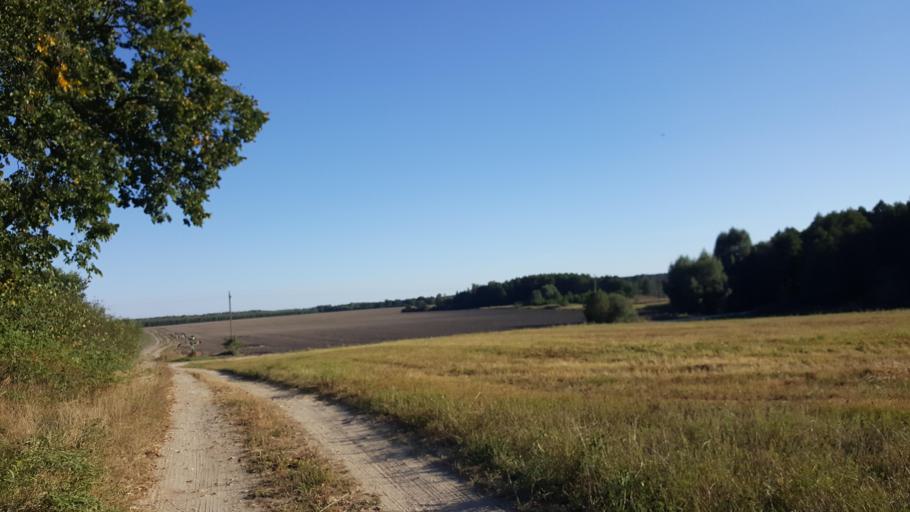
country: BY
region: Brest
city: Vysokaye
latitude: 52.3319
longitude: 23.2982
